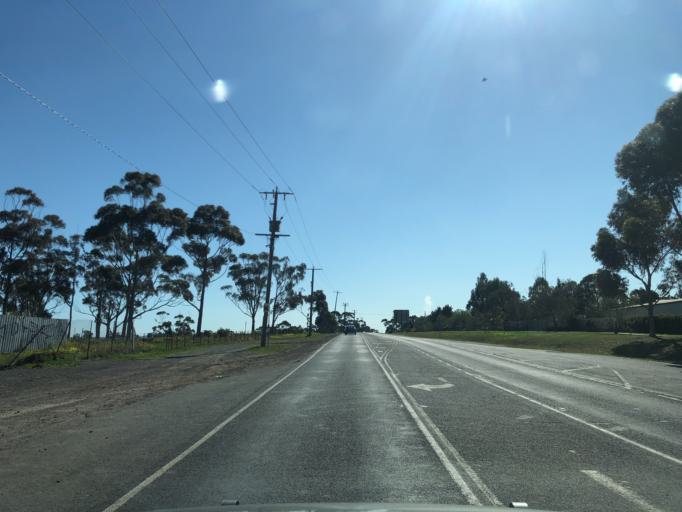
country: AU
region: Victoria
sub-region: Hume
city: Diggers Rest
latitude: -37.6353
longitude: 144.7270
